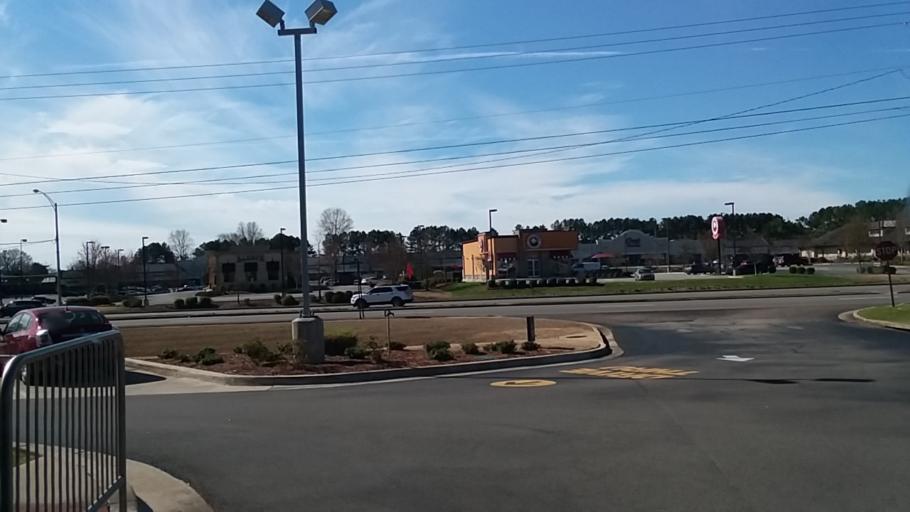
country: US
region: Alabama
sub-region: Madison County
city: Redstone Arsenal
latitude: 34.7440
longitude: -86.6750
